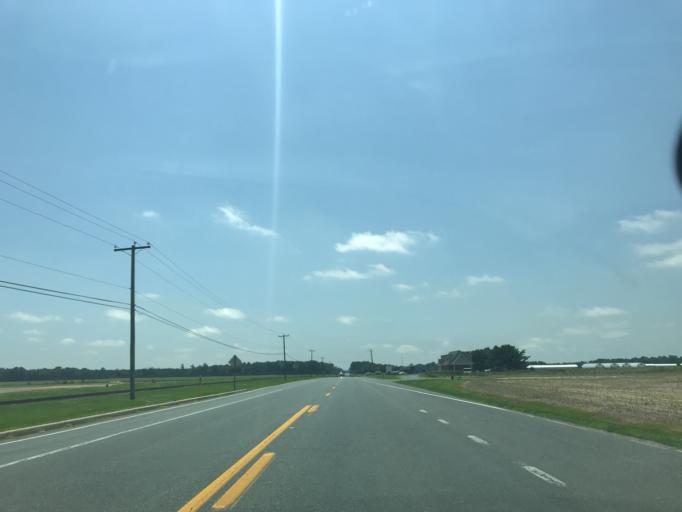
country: US
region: Maryland
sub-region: Dorchester County
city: Hurlock
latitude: 38.6280
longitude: -75.8724
